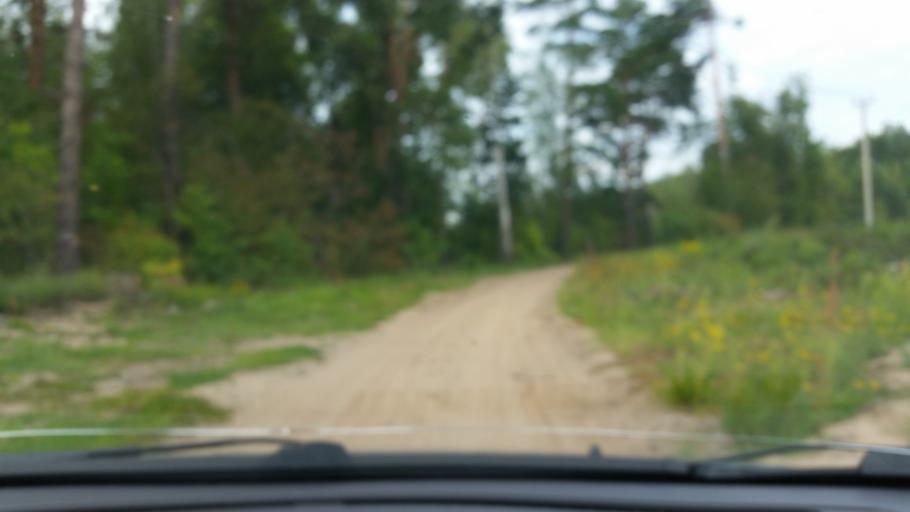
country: RU
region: Moskovskaya
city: Bol'shoye Gryzlovo
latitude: 54.8544
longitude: 37.7138
